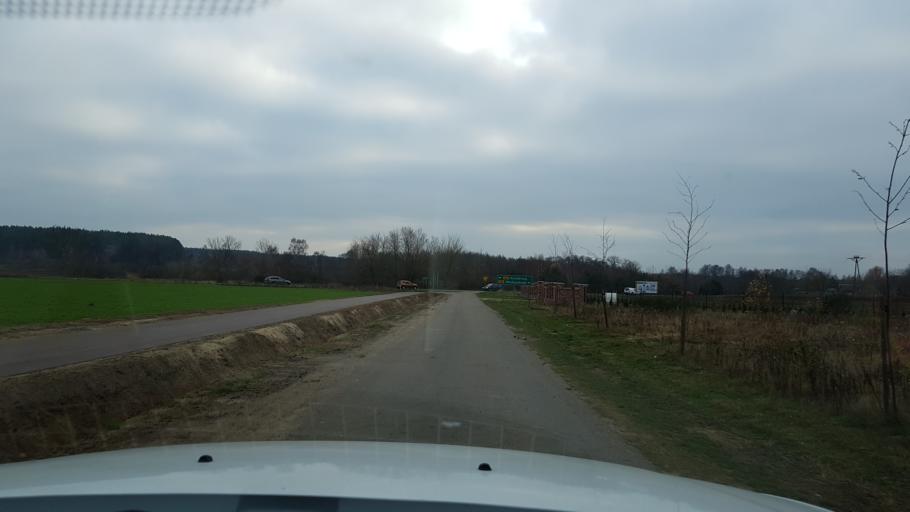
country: PL
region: West Pomeranian Voivodeship
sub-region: Powiat kolobrzeski
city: Grzybowo
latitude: 54.1096
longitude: 15.5246
